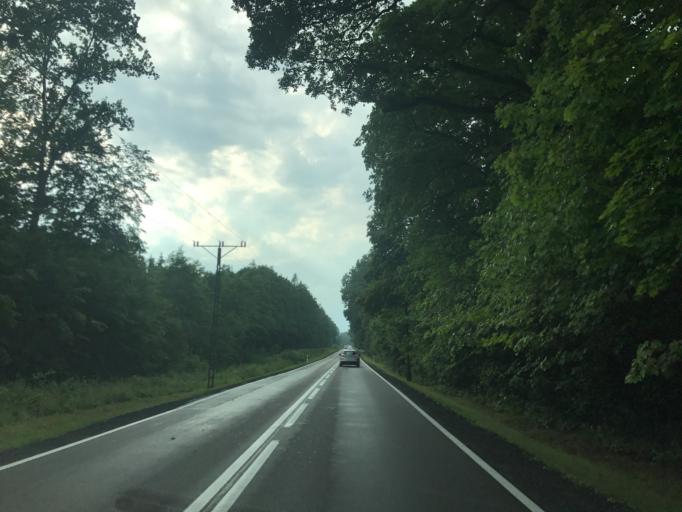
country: PL
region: Pomeranian Voivodeship
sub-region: Powiat czluchowski
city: Czluchow
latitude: 53.6917
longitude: 17.3030
